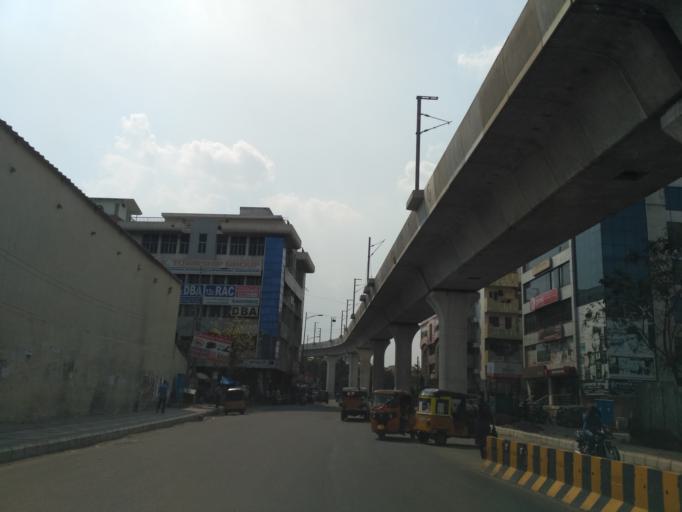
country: IN
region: Telangana
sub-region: Hyderabad
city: Hyderabad
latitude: 17.4372
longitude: 78.4421
